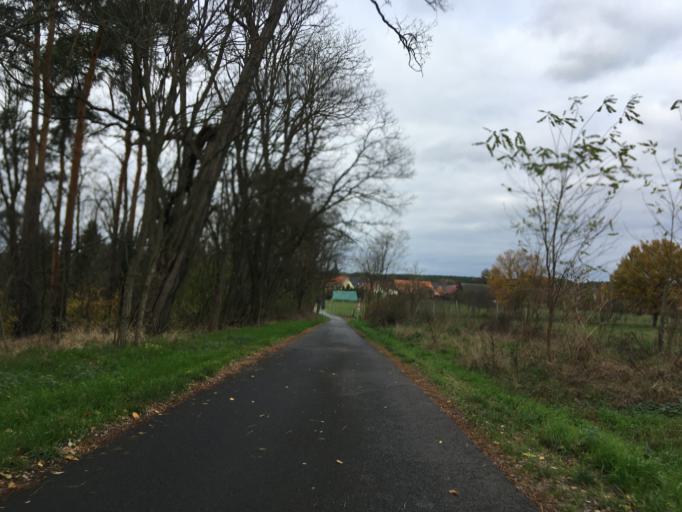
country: DE
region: Brandenburg
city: Jamlitz
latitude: 52.0876
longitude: 14.4354
